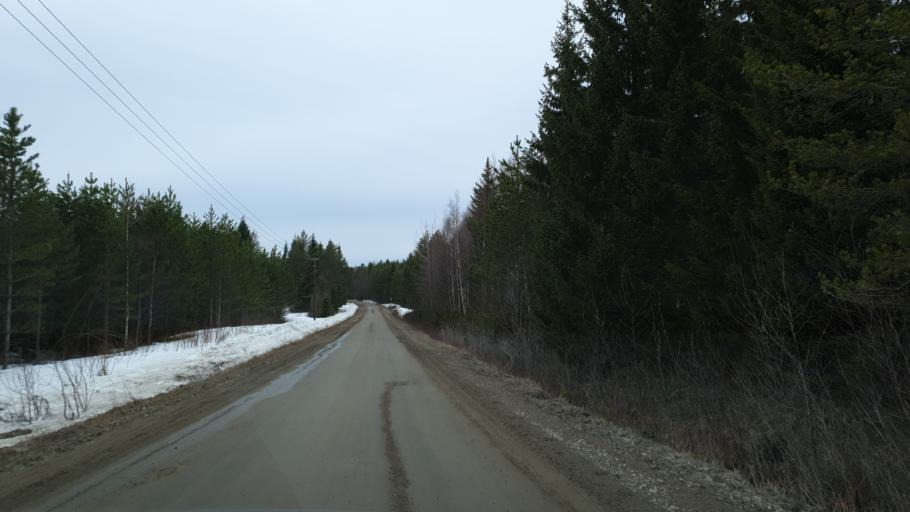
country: SE
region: Vaesterbotten
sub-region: Robertsfors Kommun
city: Robertsfors
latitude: 64.3887
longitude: 20.9556
